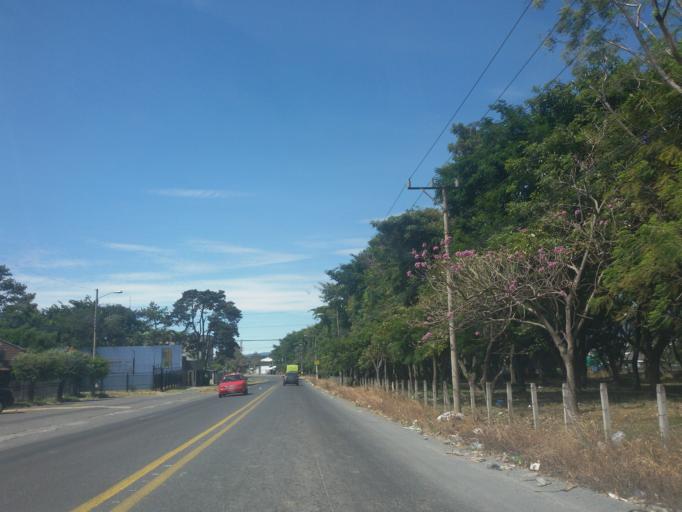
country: CR
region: Heredia
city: San Francisco
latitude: 9.9592
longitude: -84.1209
